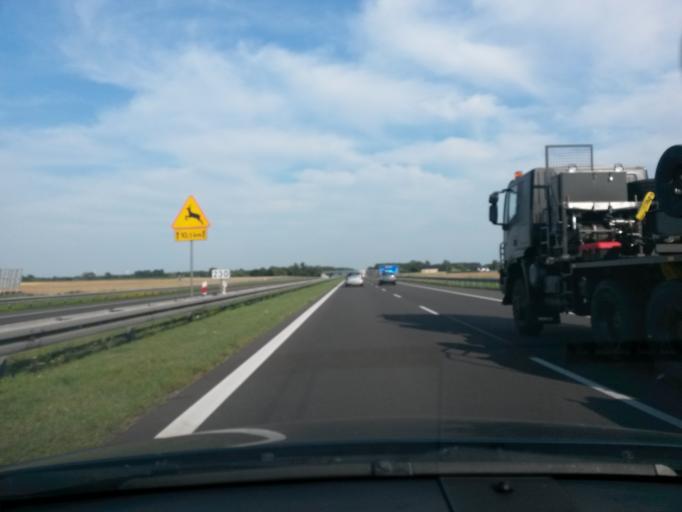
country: PL
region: Greater Poland Voivodeship
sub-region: Powiat slupecki
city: Slupca
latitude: 52.2507
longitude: 17.8360
